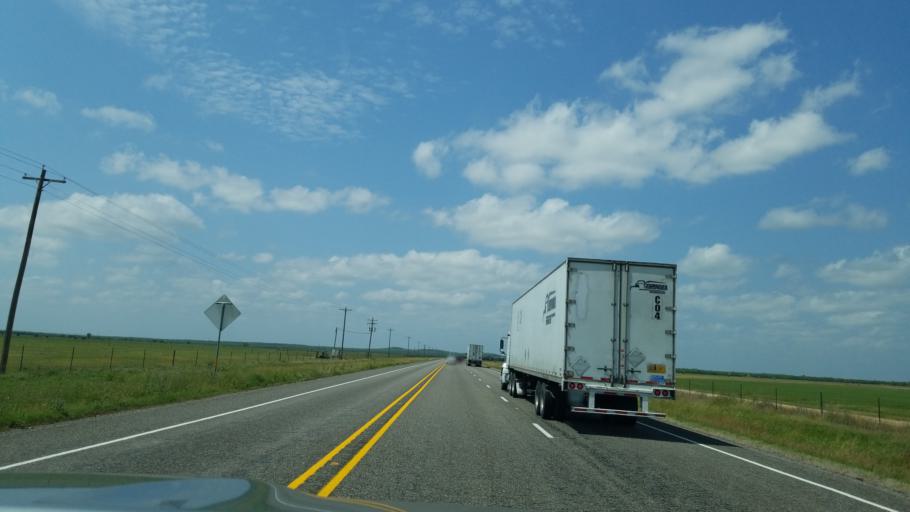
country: US
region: Texas
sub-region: Frio County
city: Pearsall
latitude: 28.9689
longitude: -99.2475
